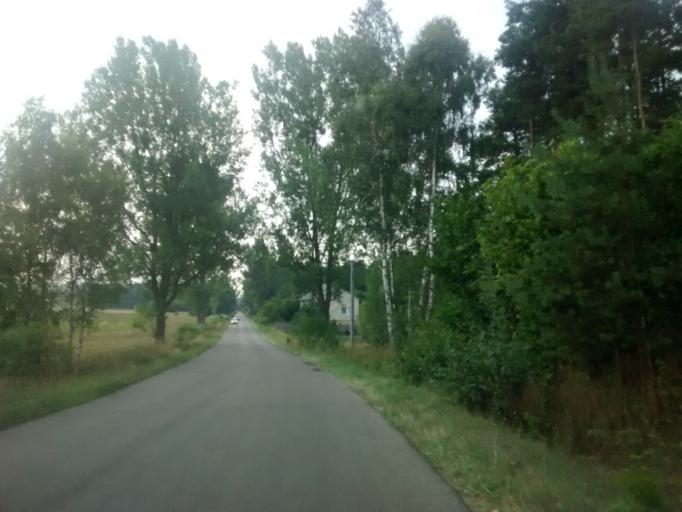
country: PL
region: Silesian Voivodeship
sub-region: Powiat zawiercianski
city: Kroczyce
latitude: 50.4956
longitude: 19.5709
